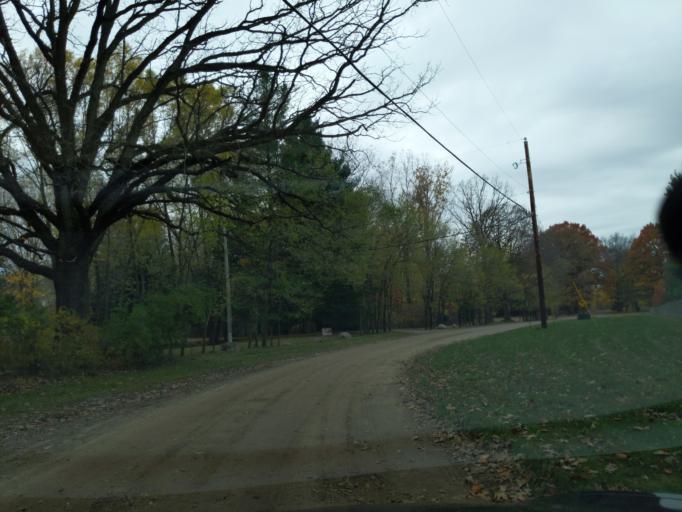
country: US
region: Michigan
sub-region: Eaton County
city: Eaton Rapids
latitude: 42.5459
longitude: -84.6180
